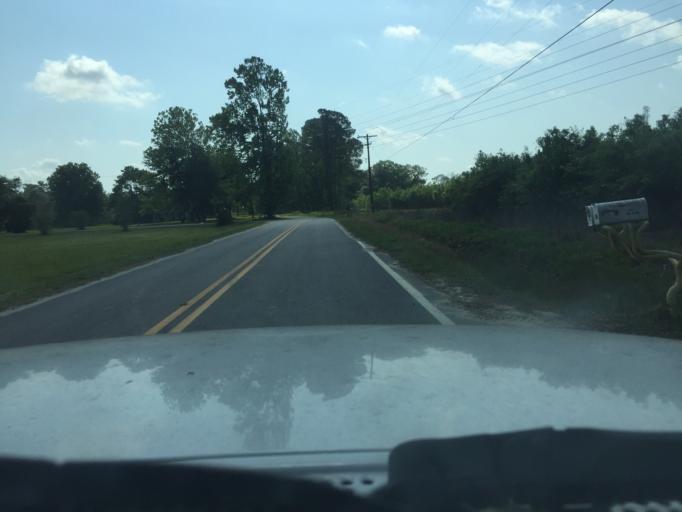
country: US
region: Georgia
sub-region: Chatham County
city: Georgetown
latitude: 32.0209
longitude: -81.2110
